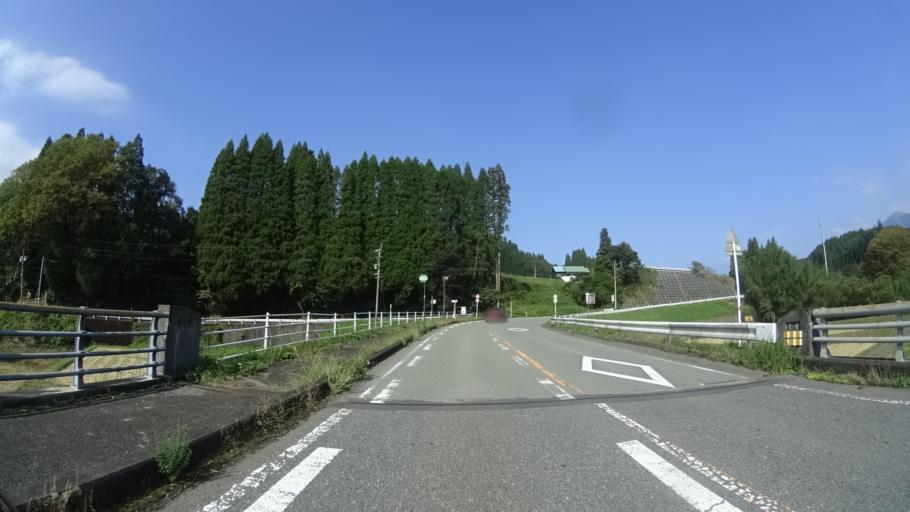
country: JP
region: Oita
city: Tsukawaki
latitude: 33.1406
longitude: 131.1021
